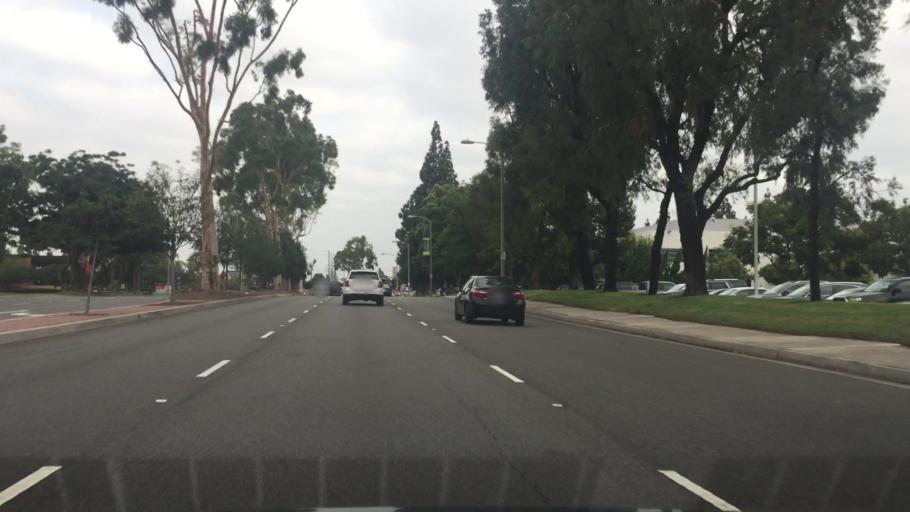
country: US
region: California
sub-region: Orange County
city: Cypress
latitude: 33.8061
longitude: -118.0282
